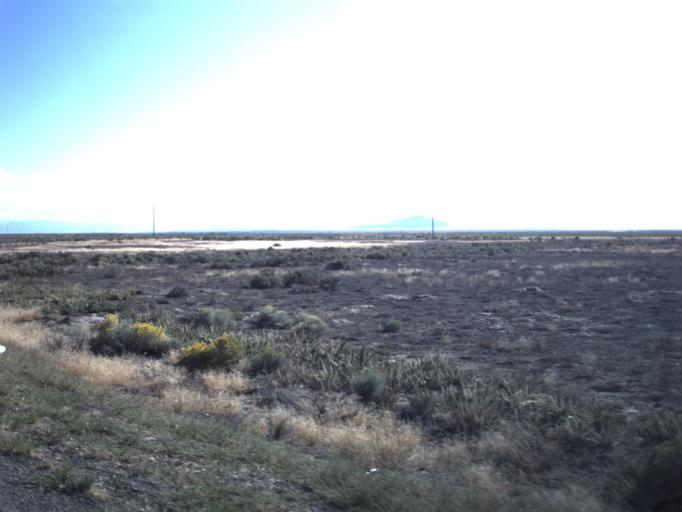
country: US
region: Utah
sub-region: Millard County
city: Delta
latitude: 39.2997
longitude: -112.4713
